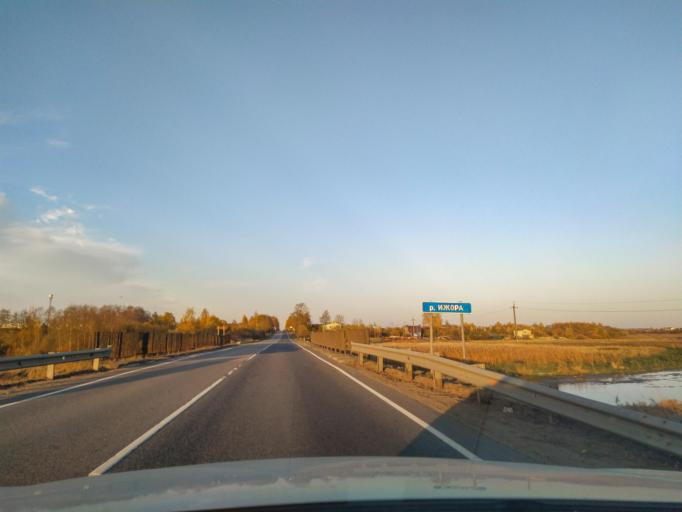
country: RU
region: Leningrad
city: Maloye Verevo
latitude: 59.6075
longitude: 30.1909
